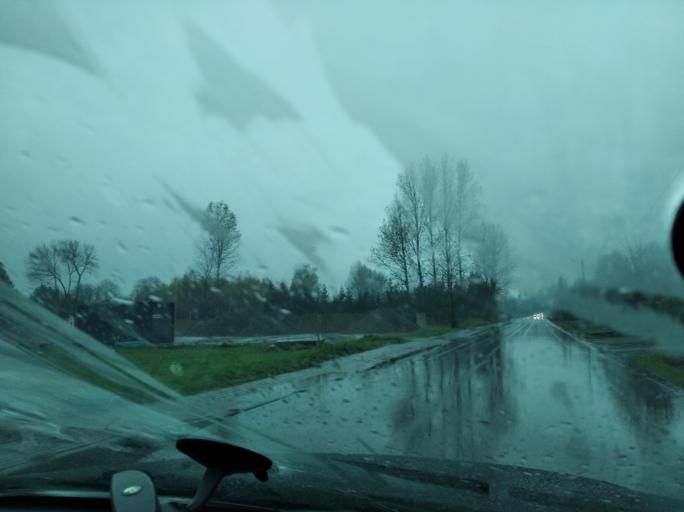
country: PL
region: Subcarpathian Voivodeship
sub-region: Powiat lancucki
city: Kraczkowa
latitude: 50.0396
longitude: 22.1893
